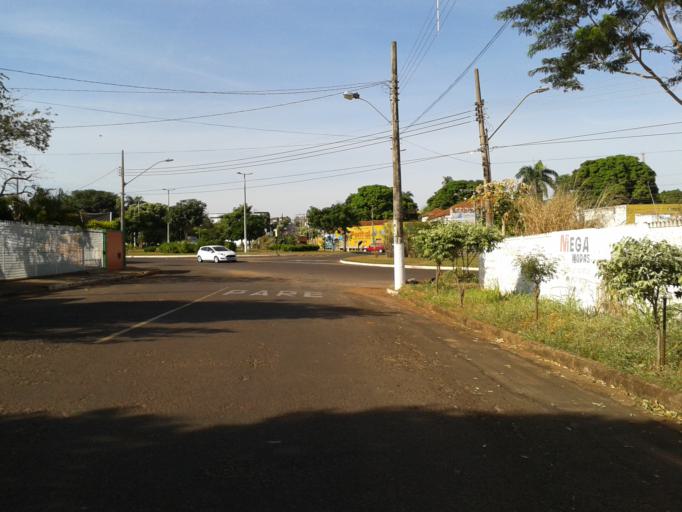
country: BR
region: Minas Gerais
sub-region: Ituiutaba
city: Ituiutaba
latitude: -18.9676
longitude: -49.4598
